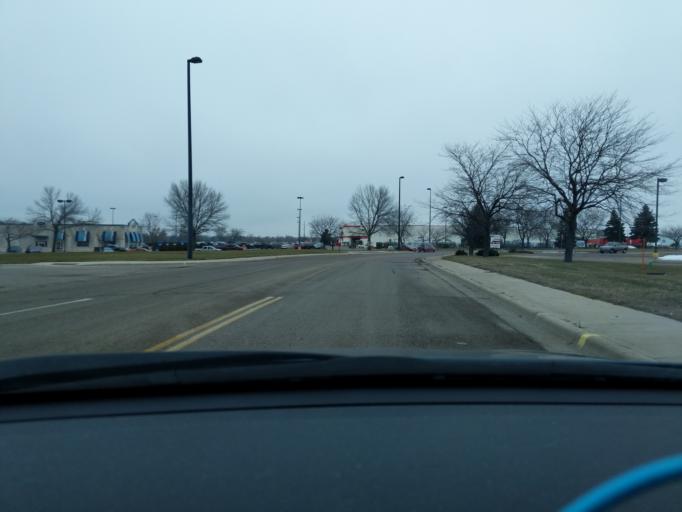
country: US
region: Minnesota
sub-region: Lyon County
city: Marshall
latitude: 44.4348
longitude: -95.7708
